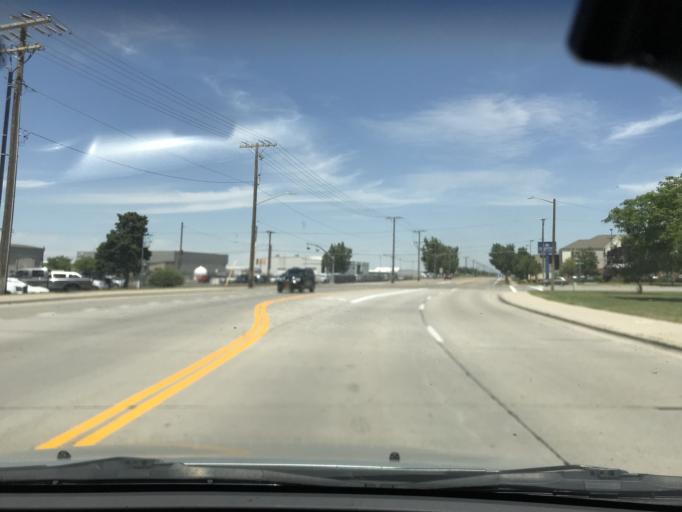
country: US
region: Utah
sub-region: Salt Lake County
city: Salt Lake City
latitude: 40.7708
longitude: -111.9534
